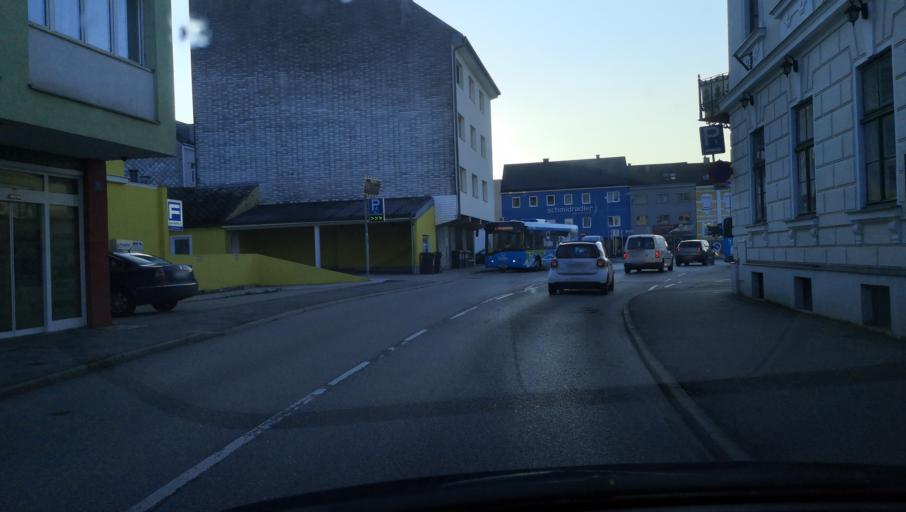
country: AT
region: Lower Austria
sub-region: Politischer Bezirk Amstetten
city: Amstetten
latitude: 48.1221
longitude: 14.8736
